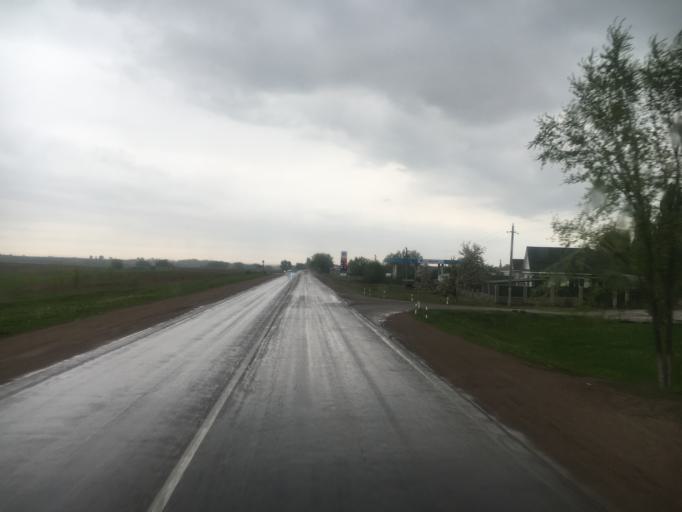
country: KZ
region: Almaty Oblysy
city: Burunday
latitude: 43.2886
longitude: 76.6734
